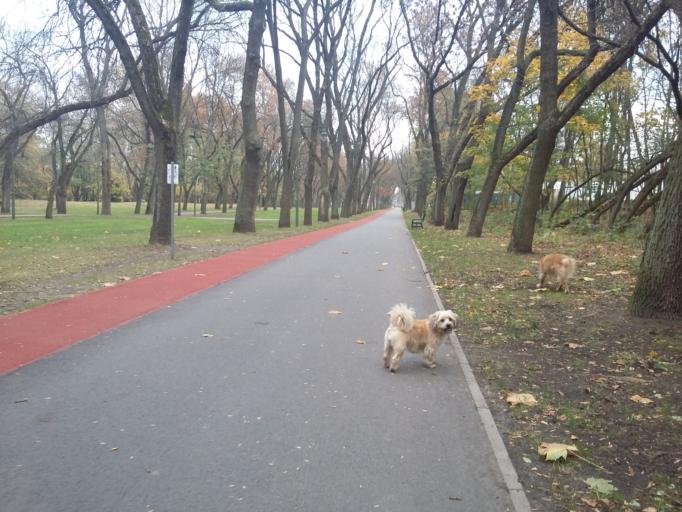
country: PL
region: Lodz Voivodeship
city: Lodz
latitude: 51.7635
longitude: 19.4188
